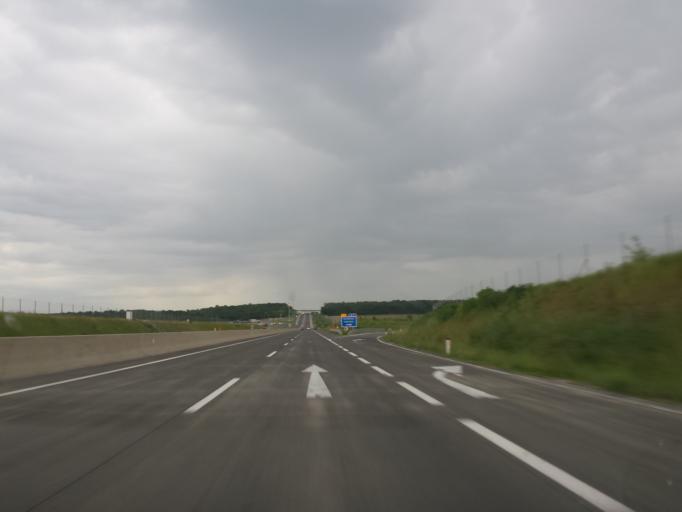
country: AT
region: Lower Austria
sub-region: Politischer Bezirk Mistelbach
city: Hochleithen
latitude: 48.4338
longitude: 16.5525
